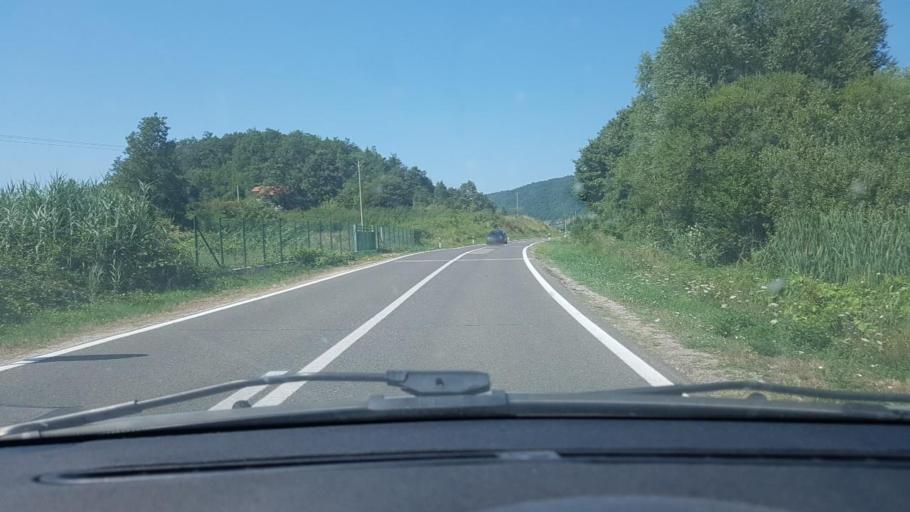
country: BA
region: Federation of Bosnia and Herzegovina
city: Bihac
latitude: 44.7611
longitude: 15.9442
